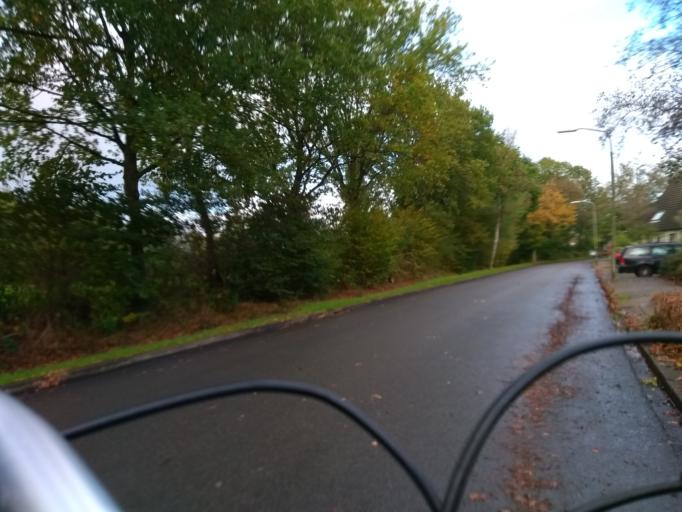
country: NL
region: Drenthe
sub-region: Gemeente Assen
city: Assen
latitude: 53.0181
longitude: 6.5684
